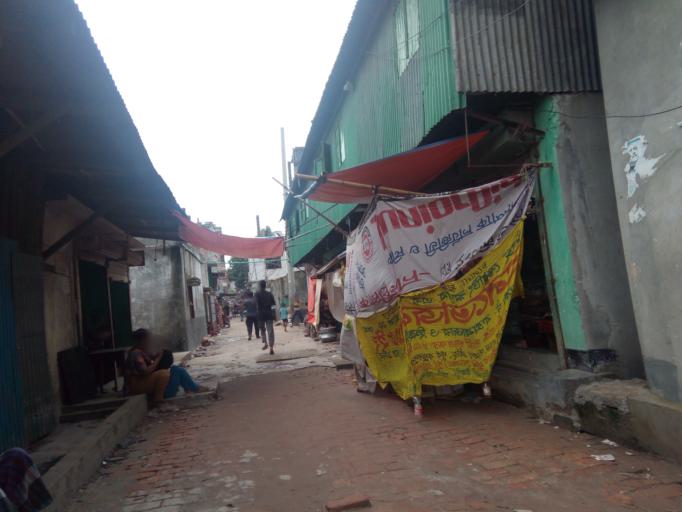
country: BD
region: Dhaka
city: Azimpur
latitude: 23.7169
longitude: 90.3743
